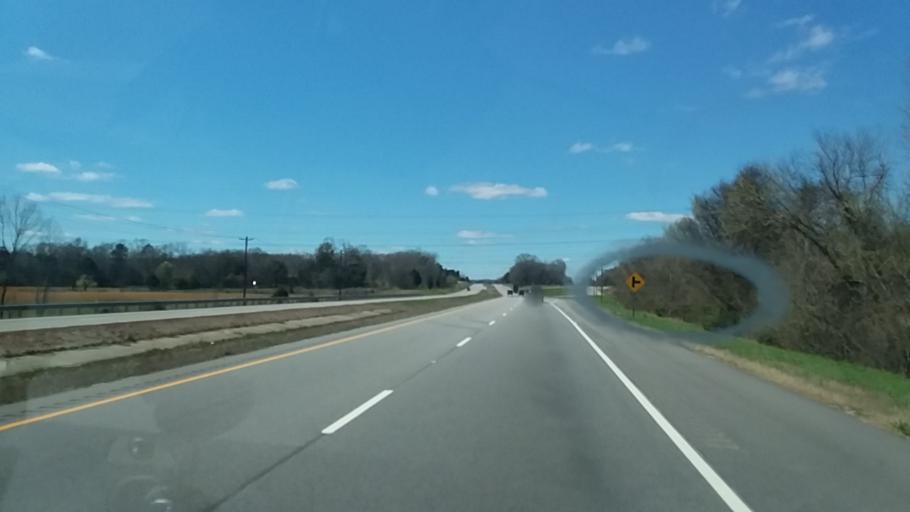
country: US
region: Alabama
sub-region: Colbert County
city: Cherokee
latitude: 34.7302
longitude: -87.8498
